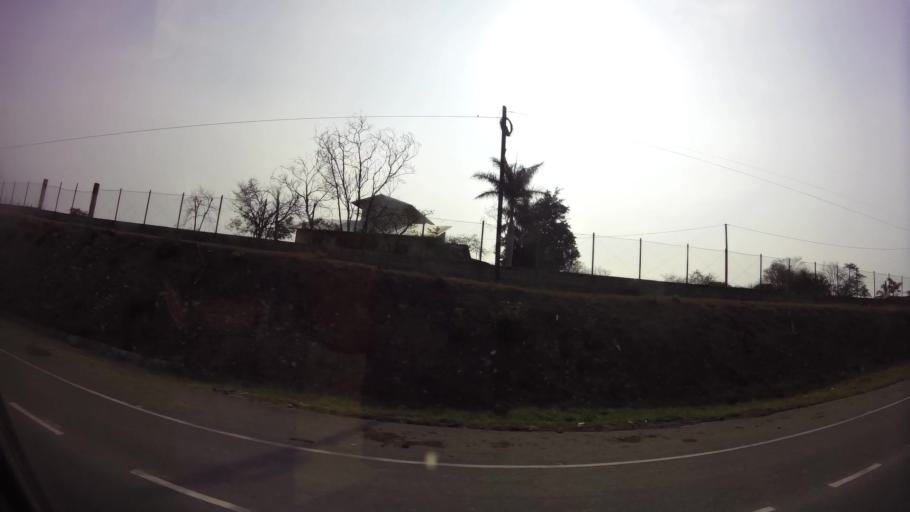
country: HN
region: Comayagua
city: Comayagua
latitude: 14.4078
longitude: -87.6212
